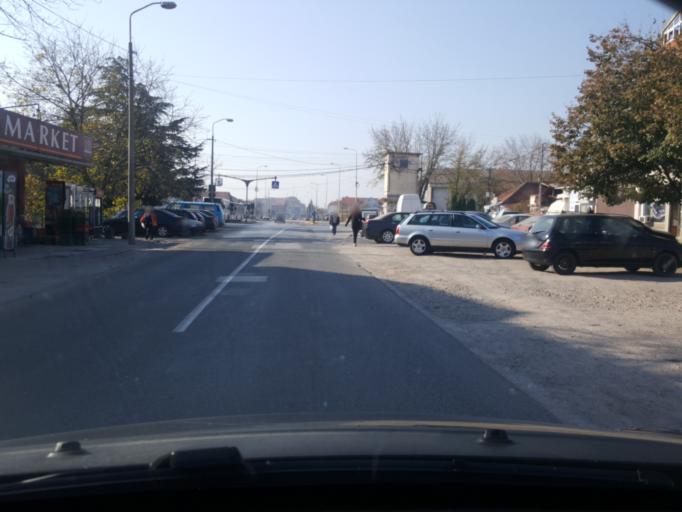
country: RS
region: Central Serbia
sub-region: Nisavski Okrug
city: Nis
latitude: 43.3306
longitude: 21.9484
